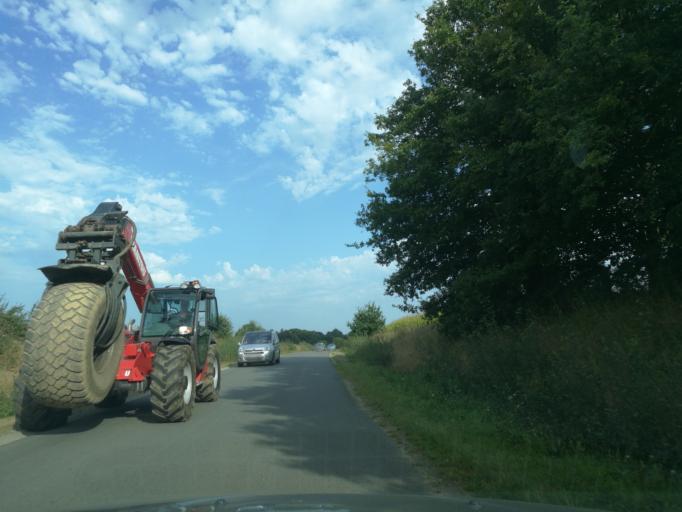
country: FR
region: Brittany
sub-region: Departement d'Ille-et-Vilaine
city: Bedee
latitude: 48.1875
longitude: -1.9533
